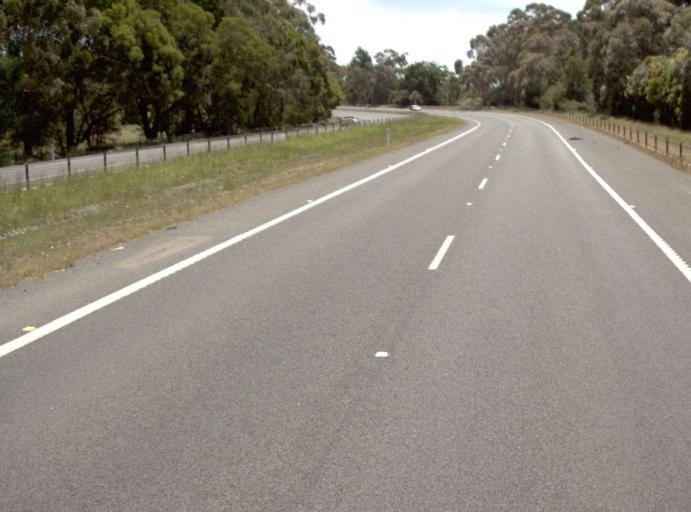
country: AU
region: Victoria
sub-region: Latrobe
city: Moe
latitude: -38.1833
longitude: 146.2753
